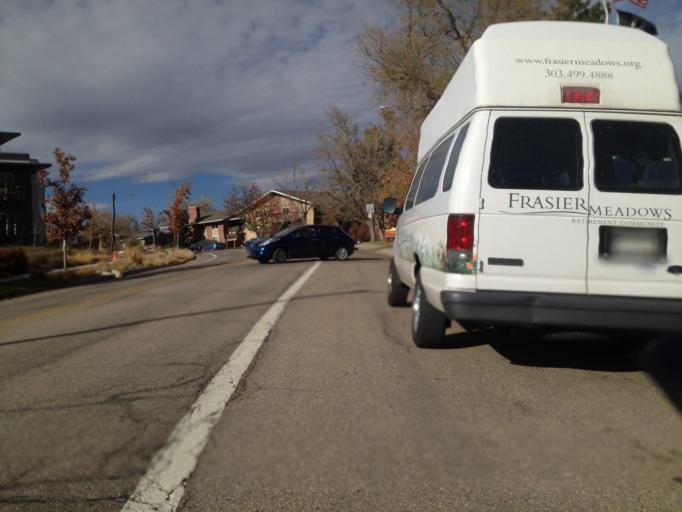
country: US
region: Colorado
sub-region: Boulder County
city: Boulder
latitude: 39.9865
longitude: -105.2376
